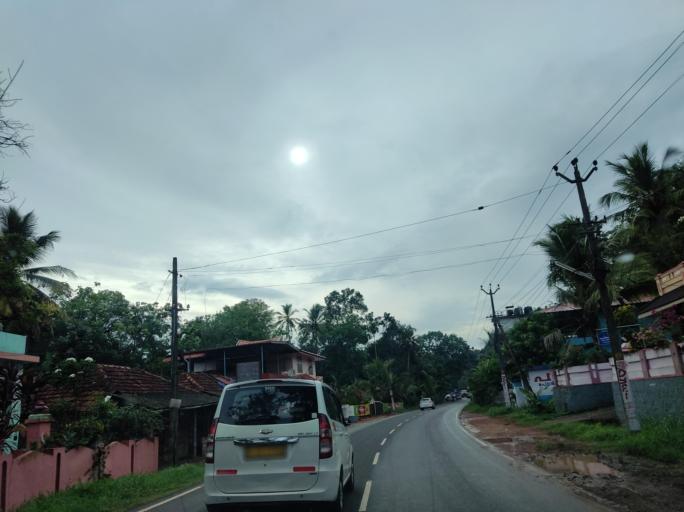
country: IN
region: Kerala
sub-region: Pattanamtitta
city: Adur
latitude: 9.1623
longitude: 76.7079
